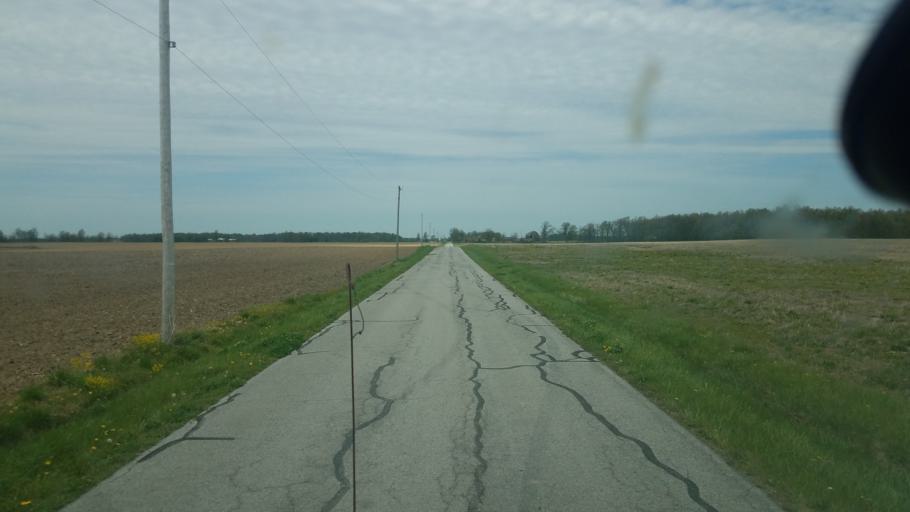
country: US
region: Ohio
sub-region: Hardin County
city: Ada
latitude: 40.8341
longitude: -83.7469
